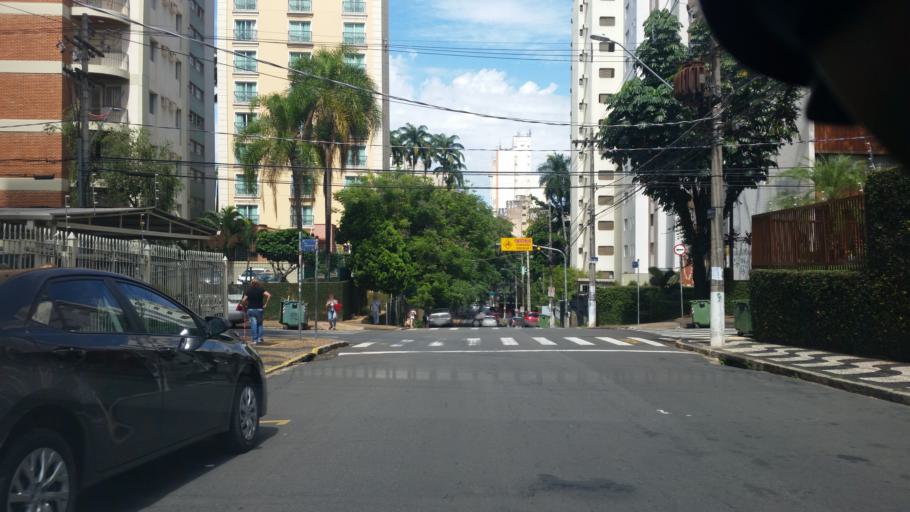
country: BR
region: Sao Paulo
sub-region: Campinas
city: Campinas
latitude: -22.9022
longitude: -47.0555
